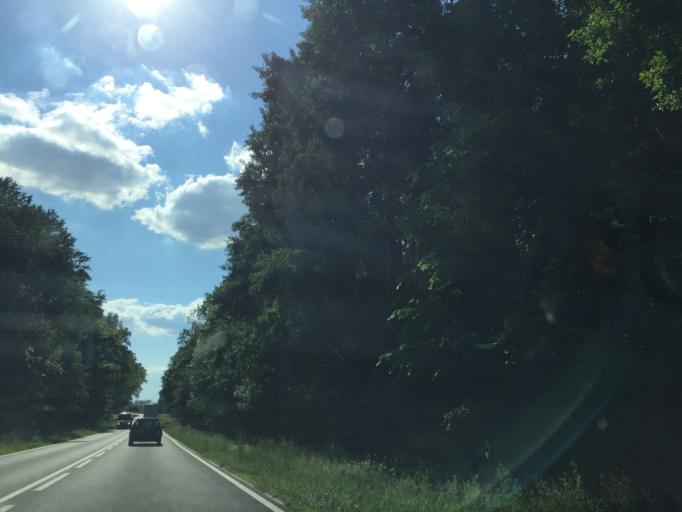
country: PL
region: Warmian-Masurian Voivodeship
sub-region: Powiat elcki
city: Stare Juchy
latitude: 53.7967
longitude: 22.2228
